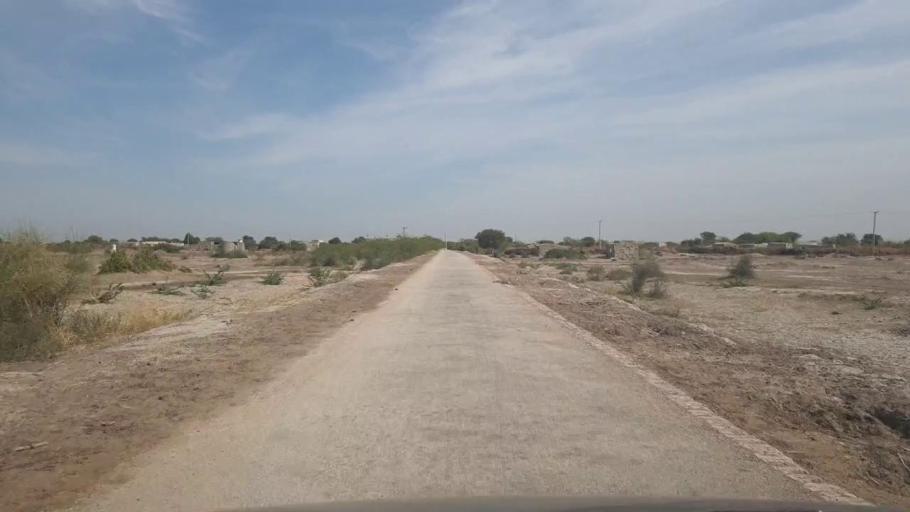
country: PK
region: Sindh
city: Kunri
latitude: 25.2123
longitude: 69.6264
